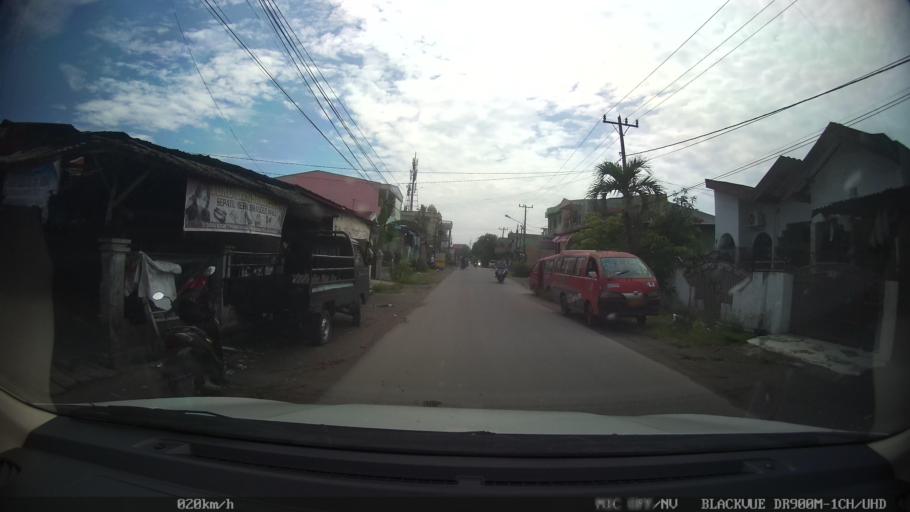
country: ID
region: North Sumatra
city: Medan
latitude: 3.5869
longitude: 98.7287
